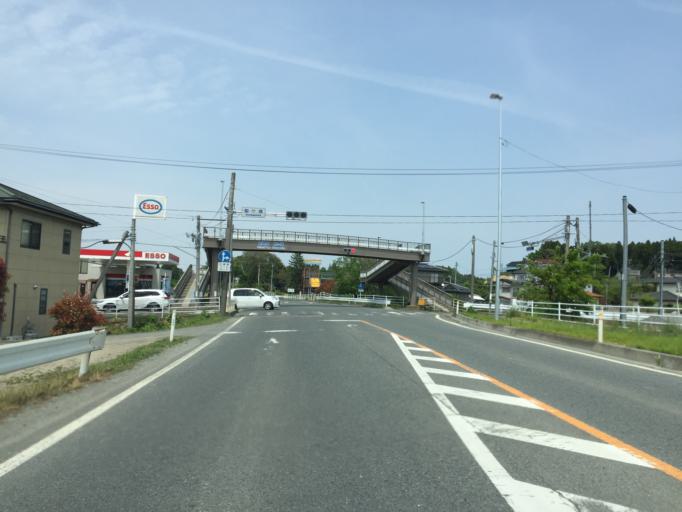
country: JP
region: Miyagi
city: Marumori
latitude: 37.8471
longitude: 140.9204
